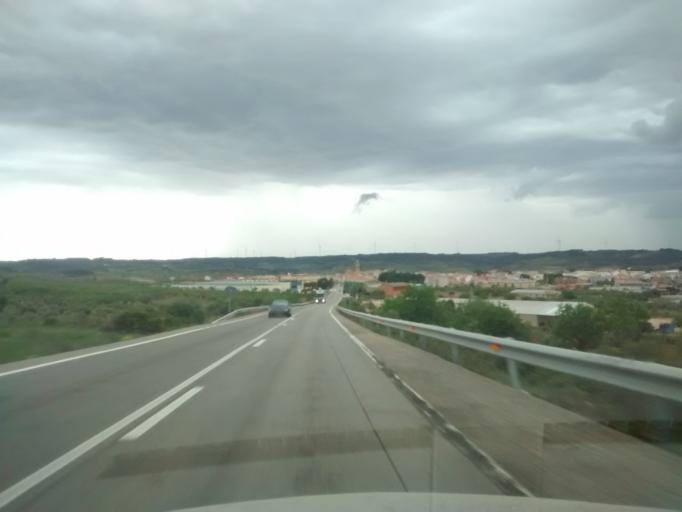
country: ES
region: Catalonia
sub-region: Provincia de Tarragona
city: Gandesa
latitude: 41.0471
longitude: 0.4507
